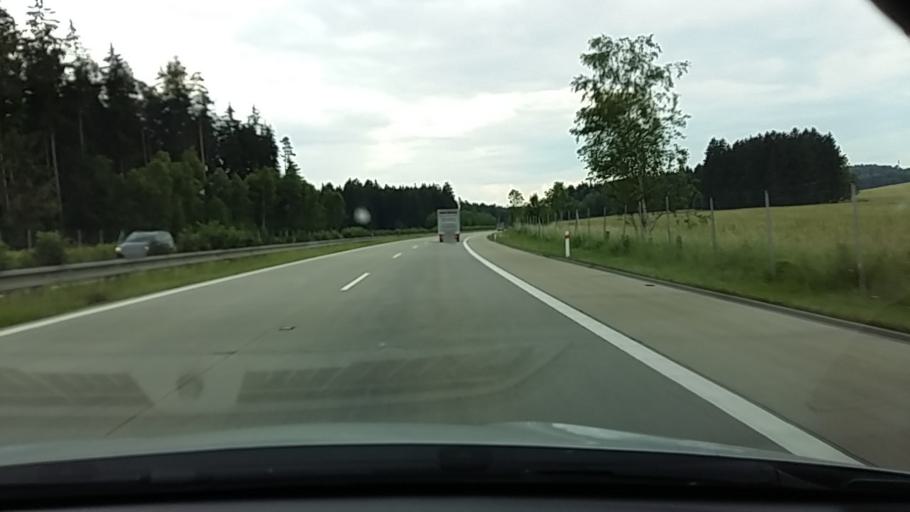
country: DE
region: Bavaria
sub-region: Upper Palatinate
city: Waidhaus
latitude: 49.6643
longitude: 12.5789
